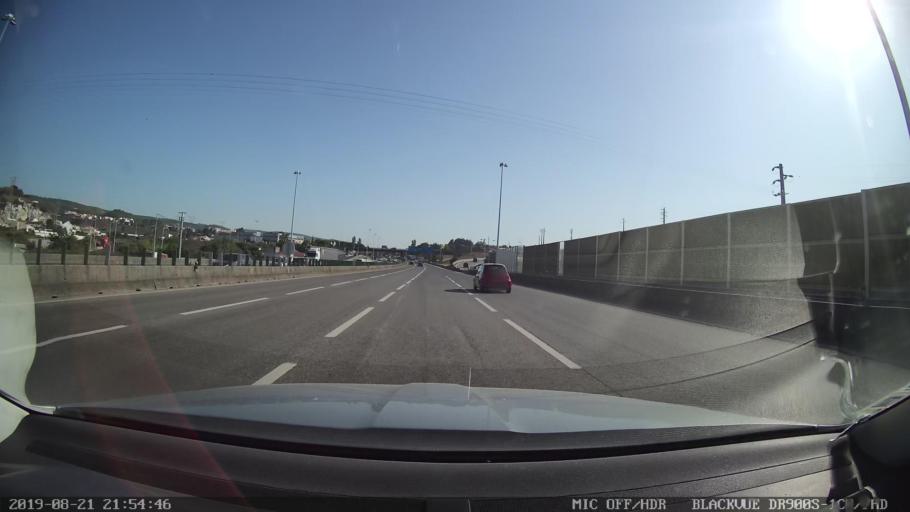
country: PT
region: Lisbon
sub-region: Vila Franca de Xira
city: Vialonga
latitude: 38.8900
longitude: -9.0508
